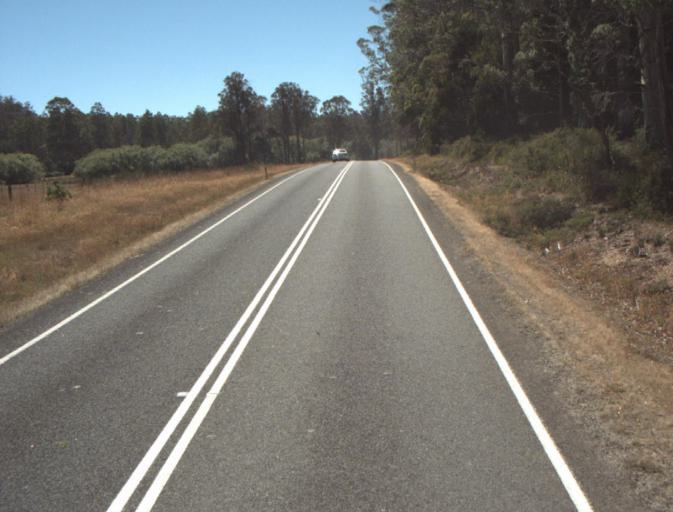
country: AU
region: Tasmania
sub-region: Dorset
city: Scottsdale
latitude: -41.3038
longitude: 147.3817
